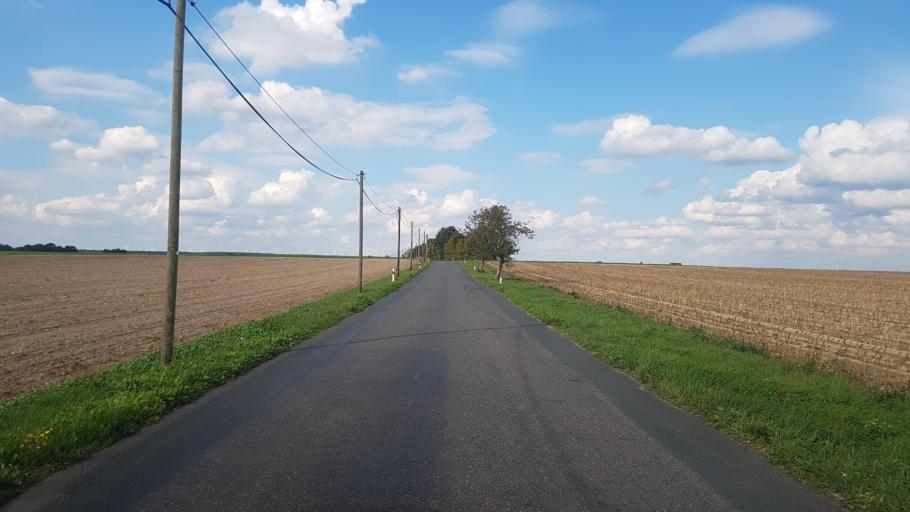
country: DE
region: Brandenburg
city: Dahme
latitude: 51.8735
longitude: 13.3833
